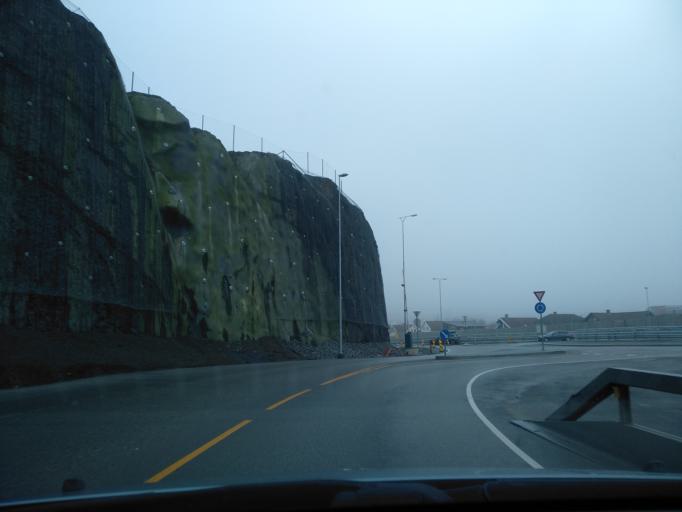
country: NO
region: Rogaland
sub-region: Stavanger
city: Stavanger
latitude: 58.9779
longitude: 5.6865
